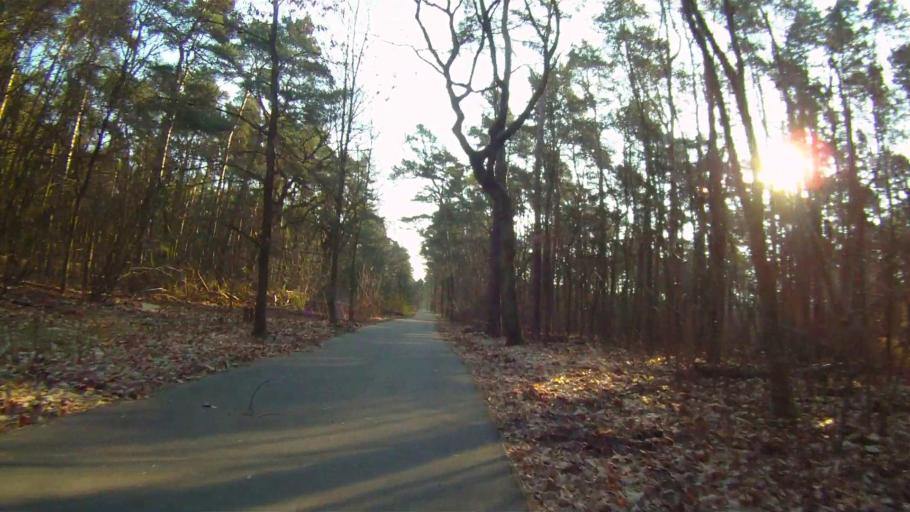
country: DE
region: Berlin
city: Friedrichshagen
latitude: 52.4259
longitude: 13.6312
